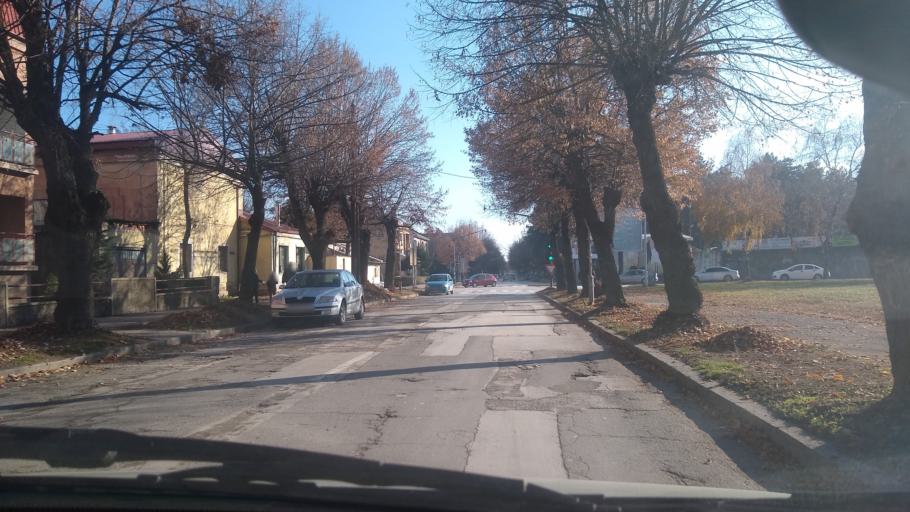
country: MK
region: Bitola
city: Bitola
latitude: 41.0242
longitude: 21.3389
